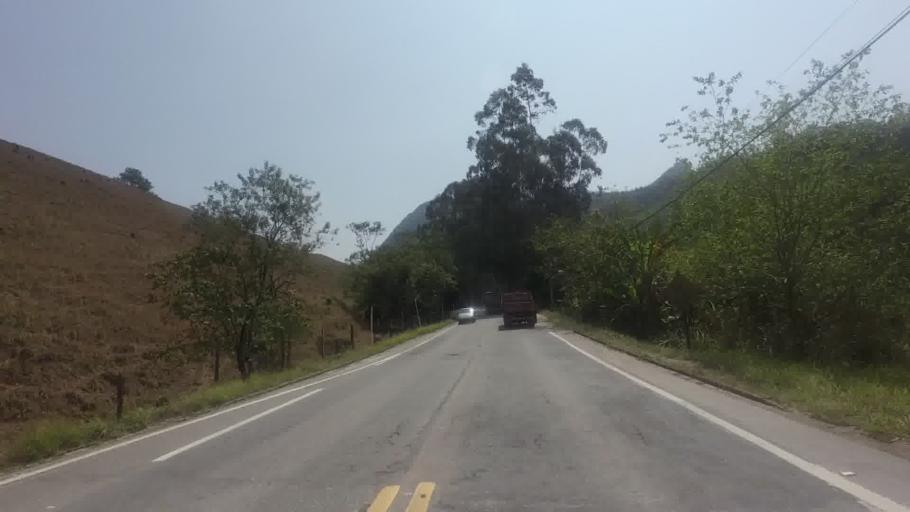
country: BR
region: Espirito Santo
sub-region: Rio Novo Do Sul
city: Rio Novo do Sul
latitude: -20.8880
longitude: -40.9960
